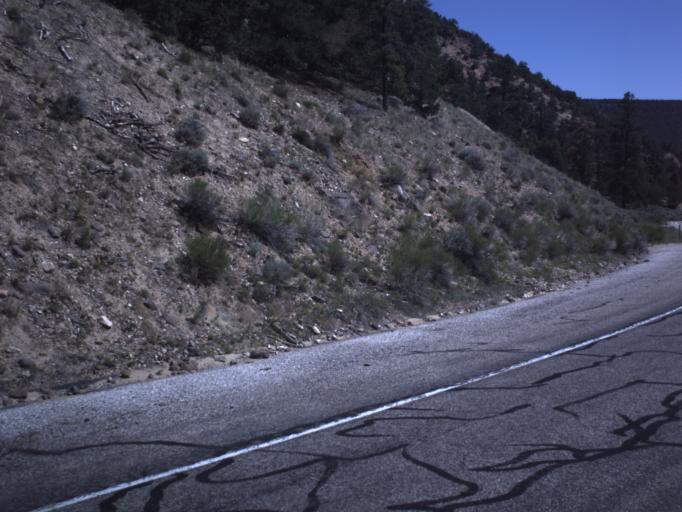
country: US
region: Utah
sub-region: Wayne County
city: Loa
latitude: 38.6593
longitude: -111.4315
